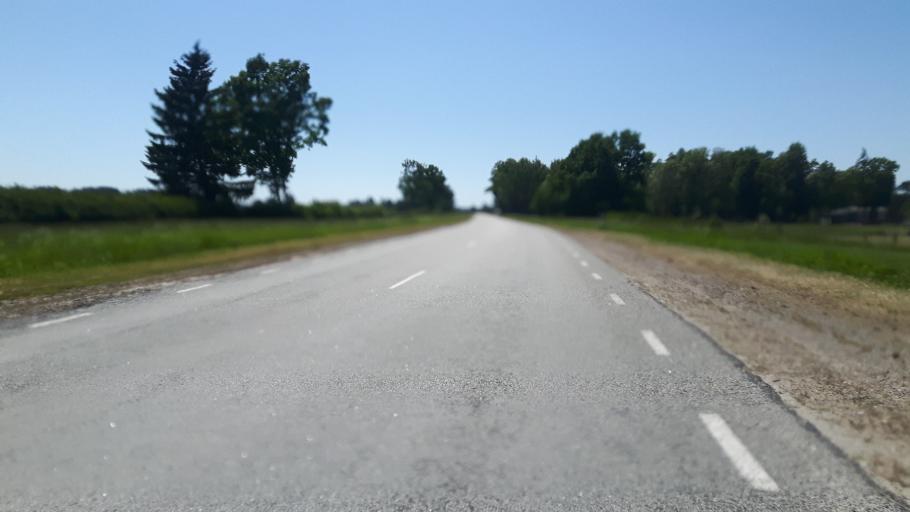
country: EE
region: Paernumaa
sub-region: Sindi linn
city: Sindi
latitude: 58.4387
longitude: 24.7414
